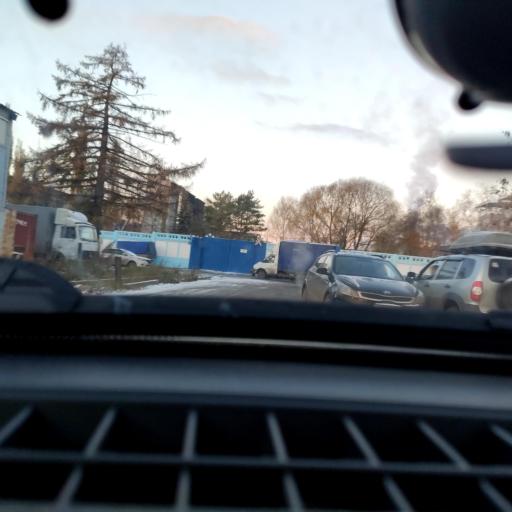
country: RU
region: Bashkortostan
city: Ufa
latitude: 54.8037
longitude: 56.0739
